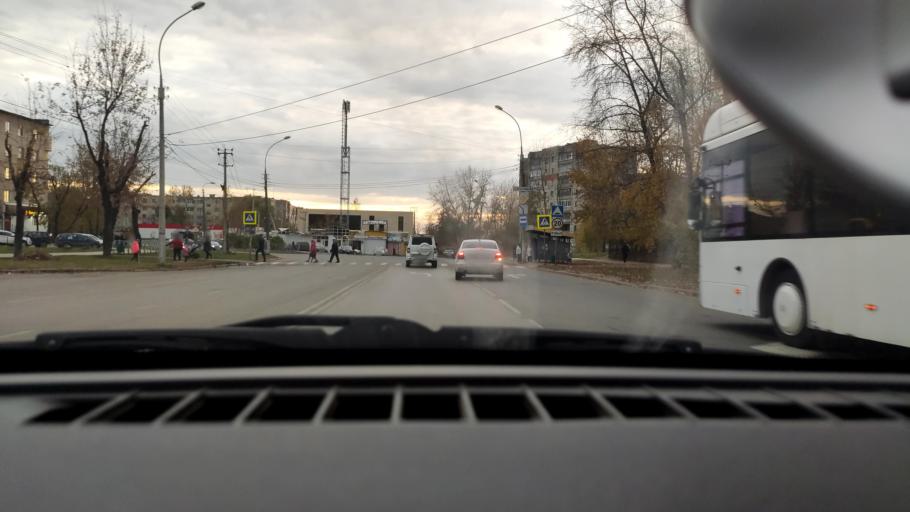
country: RU
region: Perm
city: Kondratovo
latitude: 57.9647
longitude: 56.1718
